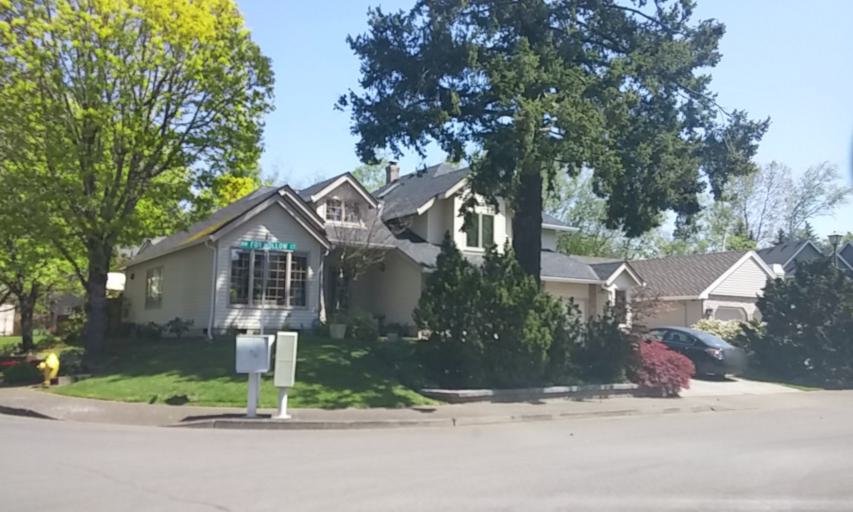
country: US
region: Oregon
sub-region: Washington County
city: West Haven
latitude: 45.5240
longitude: -122.7736
